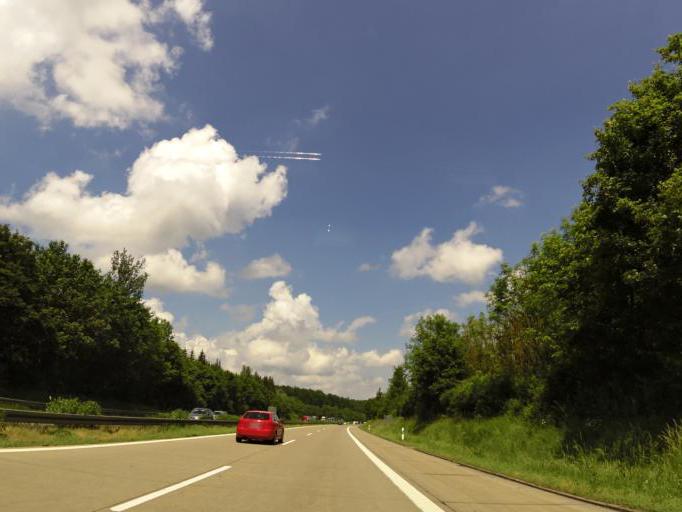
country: DE
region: Baden-Wuerttemberg
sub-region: Regierungsbezirk Stuttgart
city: Nattheim
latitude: 48.7342
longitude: 10.1984
